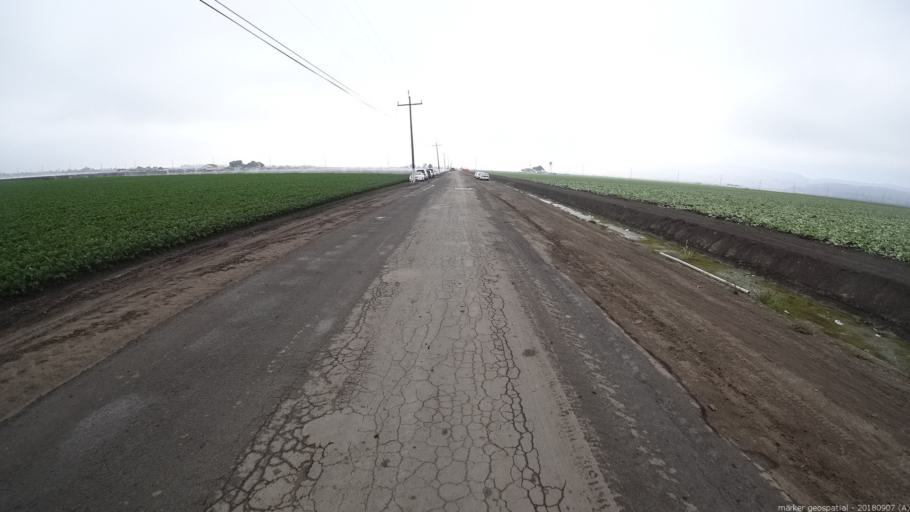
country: US
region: California
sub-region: Monterey County
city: Boronda
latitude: 36.6611
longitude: -121.6964
